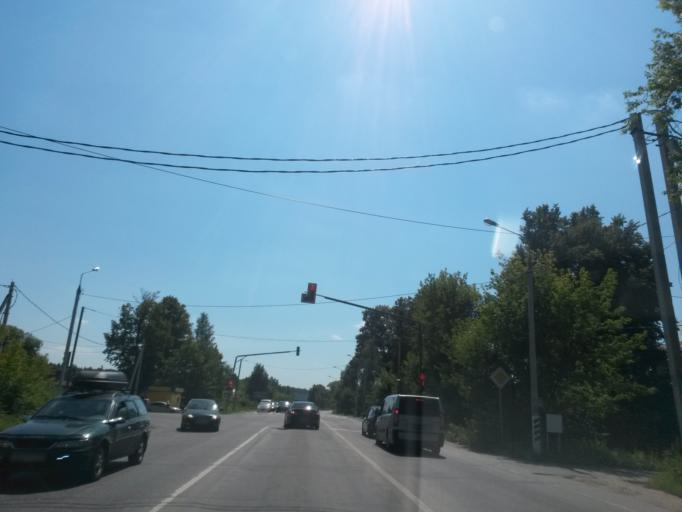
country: RU
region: Moskovskaya
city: Stolbovaya
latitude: 55.2450
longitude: 37.5043
